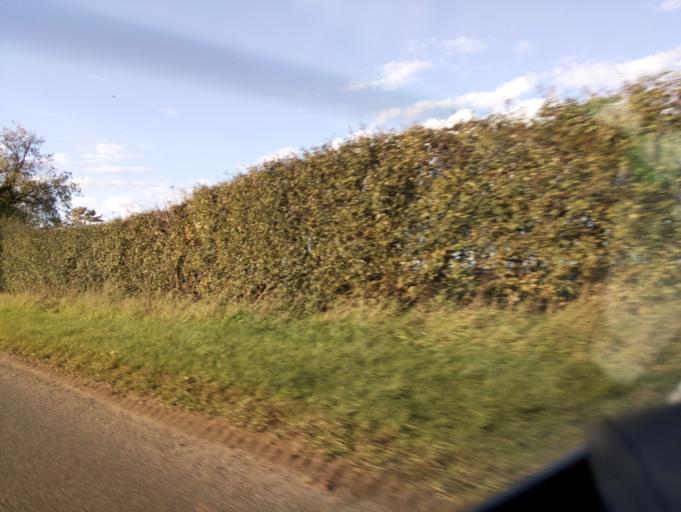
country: GB
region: England
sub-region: Herefordshire
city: Ledbury
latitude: 52.0520
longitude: -2.4808
